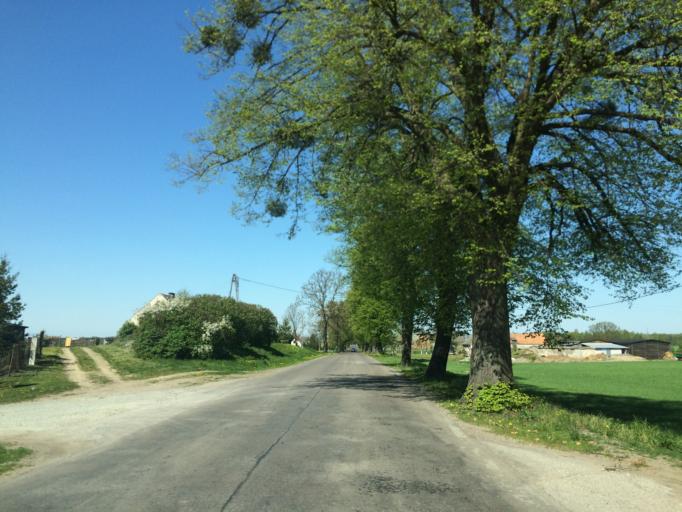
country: PL
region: Warmian-Masurian Voivodeship
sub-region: Powiat nowomiejski
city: Biskupiec
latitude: 53.4974
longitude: 19.3747
